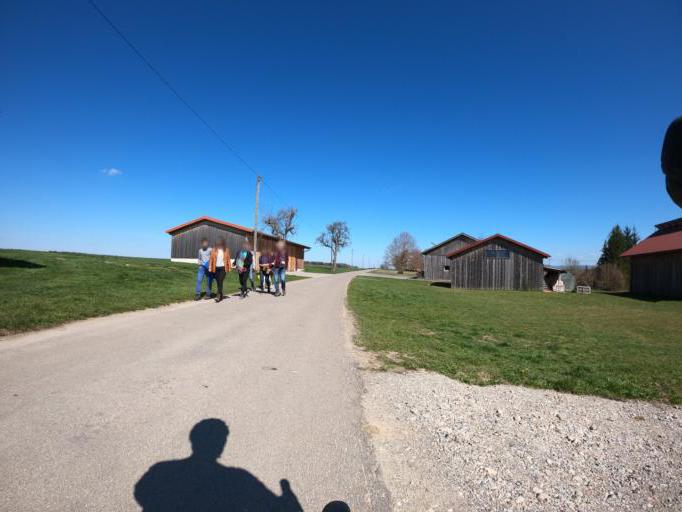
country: DE
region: Baden-Wuerttemberg
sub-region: Tuebingen Region
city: Haigerloch
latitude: 48.3876
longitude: 8.8181
